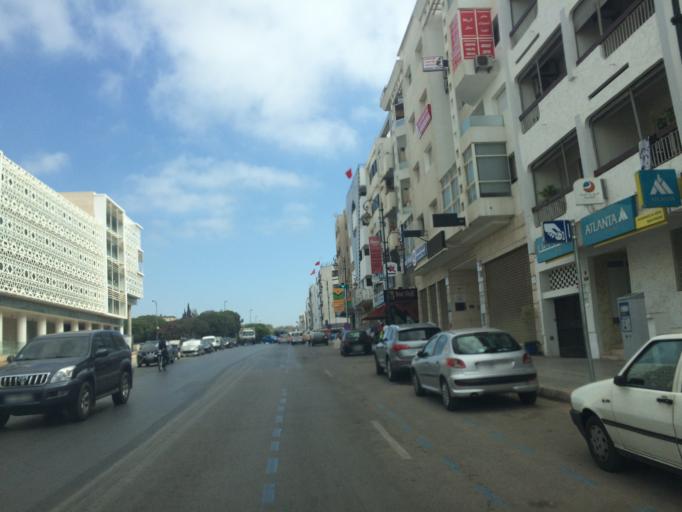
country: MA
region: Rabat-Sale-Zemmour-Zaer
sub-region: Rabat
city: Rabat
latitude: 34.0029
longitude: -6.8461
